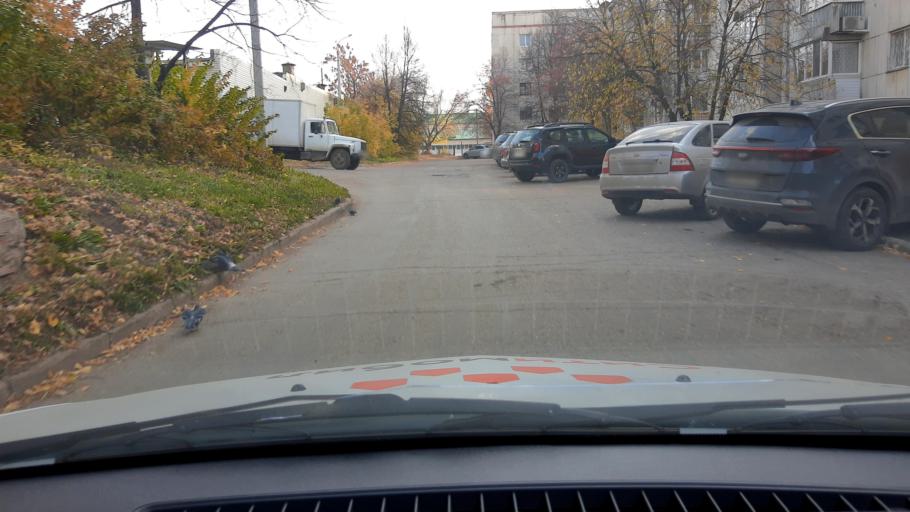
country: RU
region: Bashkortostan
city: Ufa
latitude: 54.8134
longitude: 56.0665
